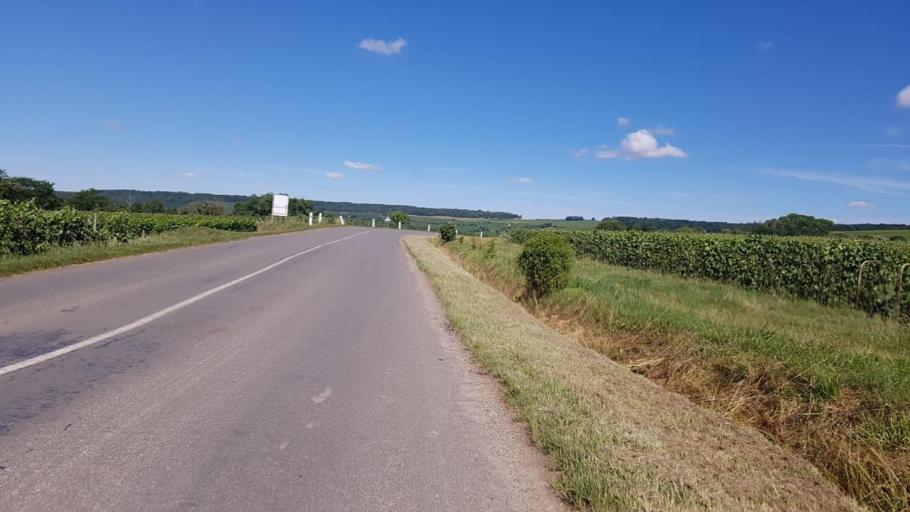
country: FR
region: Picardie
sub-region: Departement de l'Aisne
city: Charly-sur-Marne
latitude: 48.9684
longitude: 3.2586
